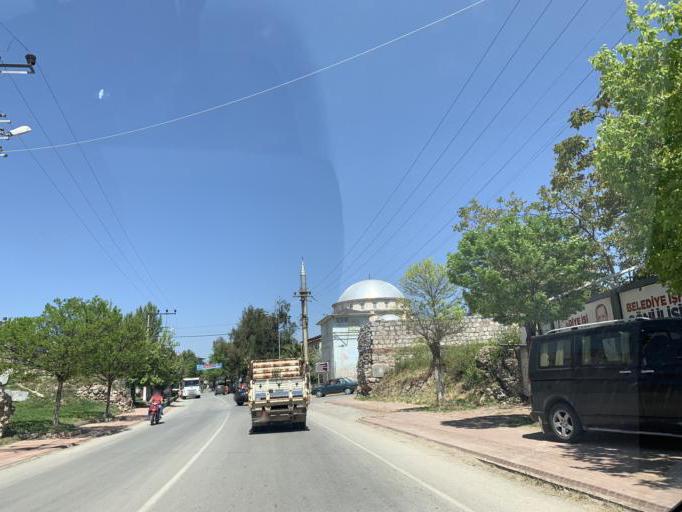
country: TR
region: Bursa
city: Iznik
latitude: 40.4231
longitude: 29.7198
